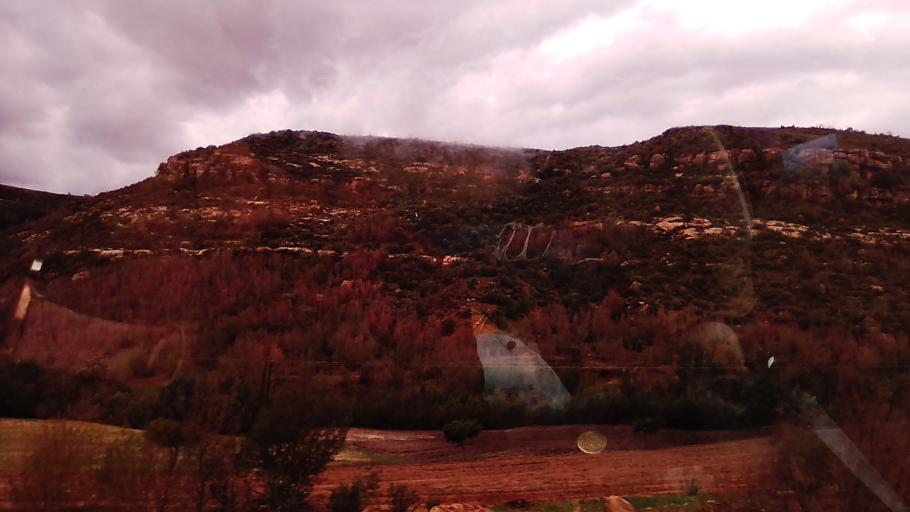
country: LS
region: Berea
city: Teyateyaneng
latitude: -29.3311
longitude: 27.7002
